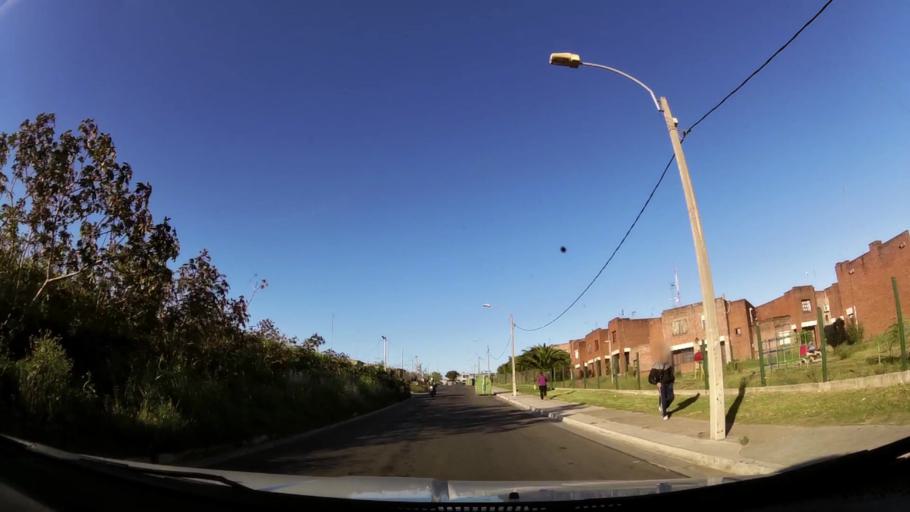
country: UY
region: Canelones
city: La Paz
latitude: -34.8307
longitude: -56.2314
